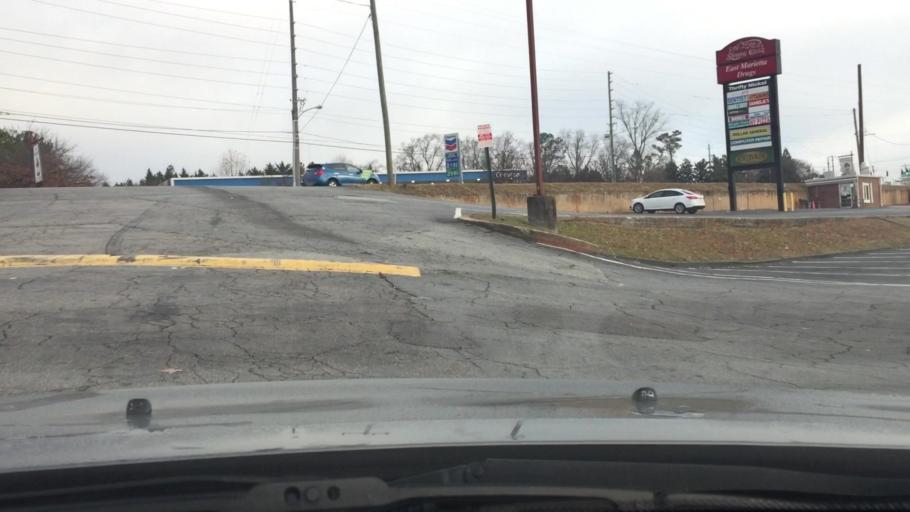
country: US
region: Georgia
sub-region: Cobb County
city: Marietta
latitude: 33.9506
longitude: -84.5091
